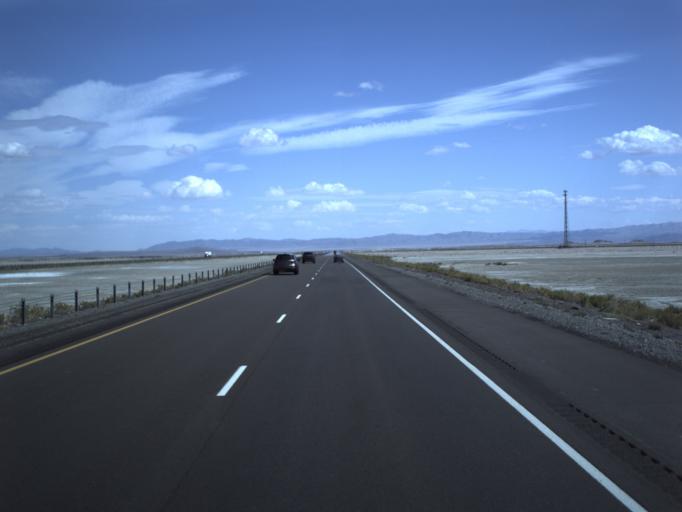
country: US
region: Utah
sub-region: Tooele County
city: Wendover
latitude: 40.7277
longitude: -113.3466
